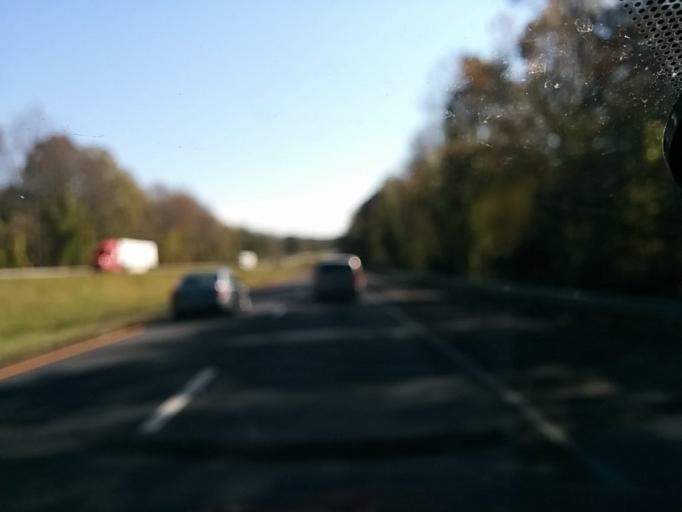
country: US
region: Virginia
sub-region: City of Charlottesville
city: Charlottesville
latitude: 38.0222
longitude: -78.5511
